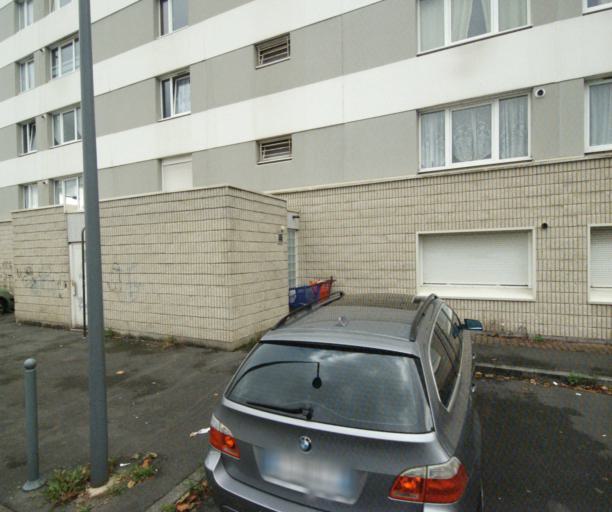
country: FR
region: Nord-Pas-de-Calais
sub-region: Departement du Nord
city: Lomme
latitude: 50.6511
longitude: 2.9896
